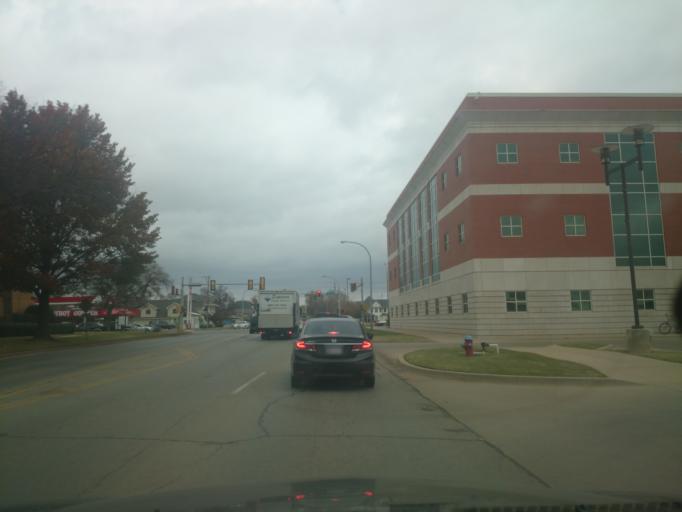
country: US
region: Oklahoma
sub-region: Payne County
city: Stillwater
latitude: 36.1149
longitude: -97.0626
